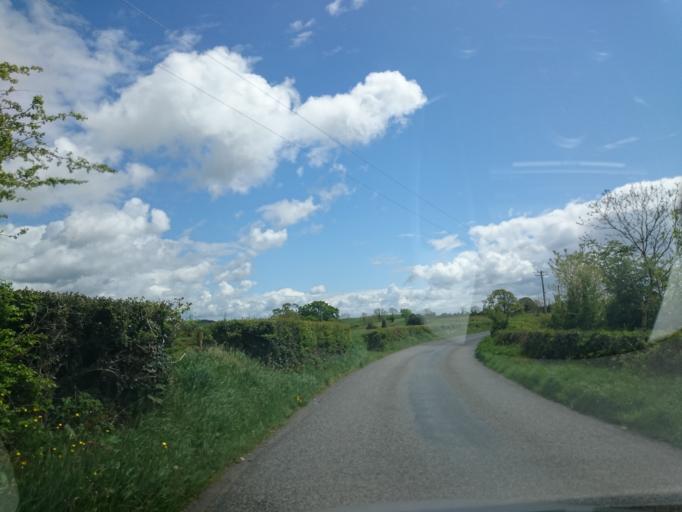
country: IE
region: Leinster
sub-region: Laois
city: Mountrath
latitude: 53.0322
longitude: -7.5403
